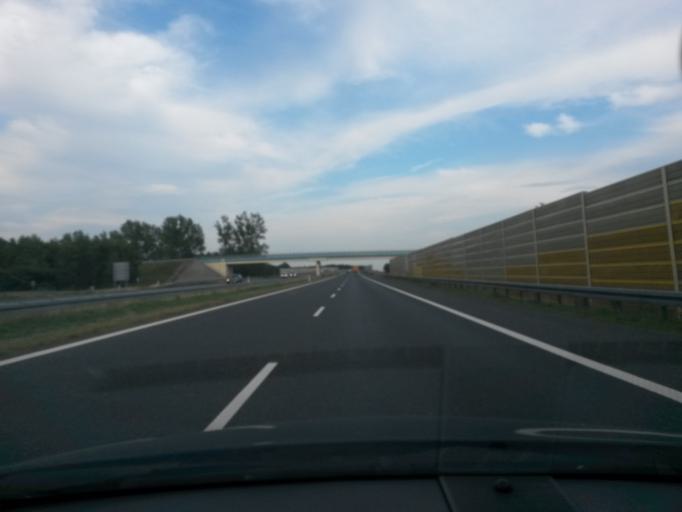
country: PL
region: Lodz Voivodeship
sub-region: Powiat leczycki
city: Swinice Warckie
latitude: 52.0285
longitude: 18.9039
